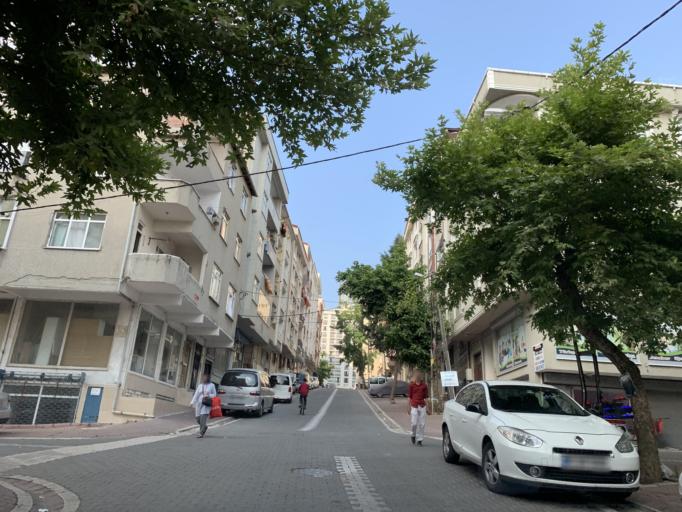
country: TR
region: Istanbul
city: Esenyurt
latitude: 41.0290
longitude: 28.6783
